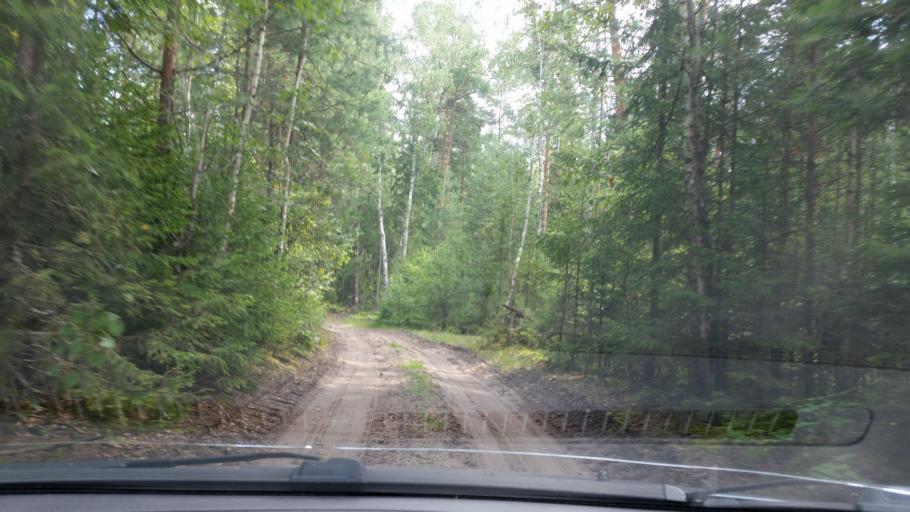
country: RU
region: Moskovskaya
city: Pushchino
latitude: 54.9234
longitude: 37.6886
